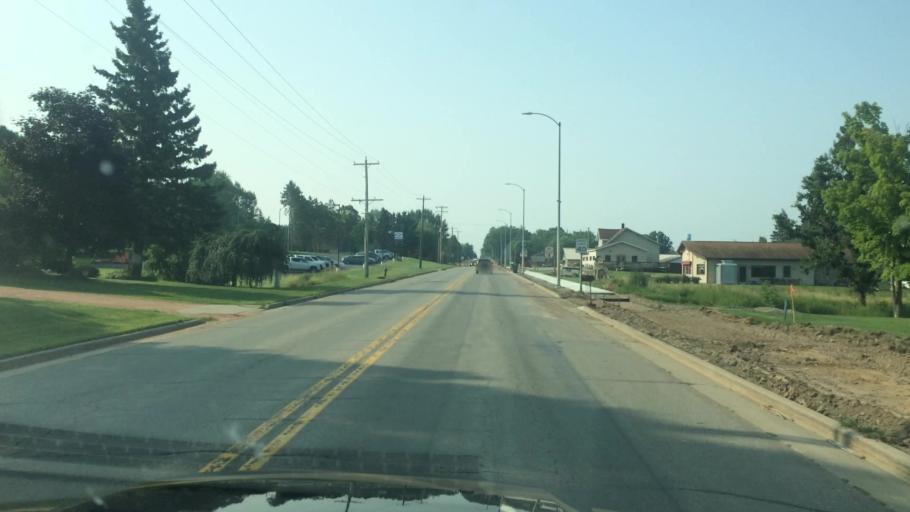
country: US
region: Wisconsin
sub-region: Marathon County
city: Stratford
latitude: 44.8107
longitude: -90.0792
